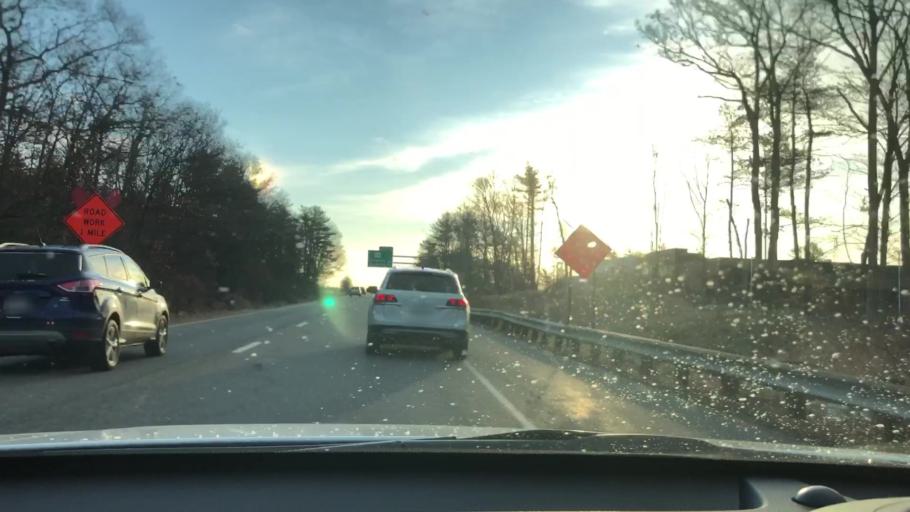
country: US
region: Massachusetts
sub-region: Plymouth County
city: Rockland
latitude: 42.1686
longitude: -70.9008
